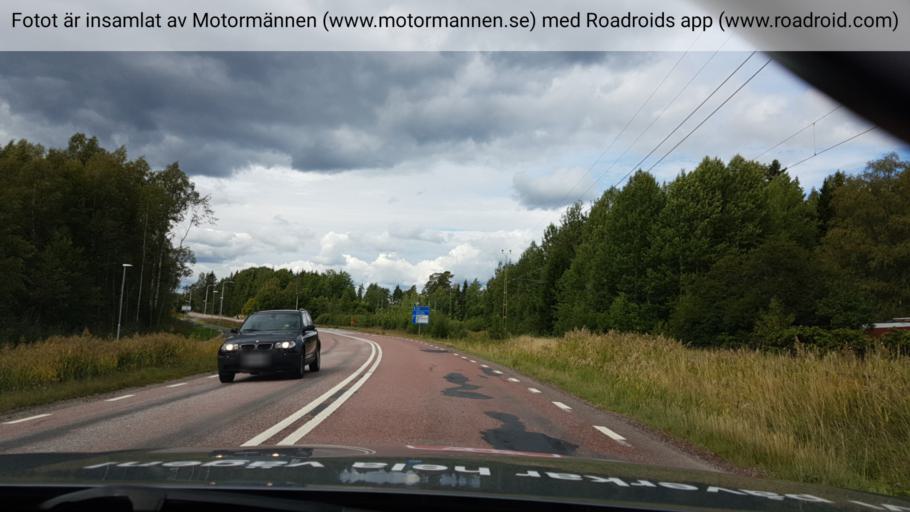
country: SE
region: Uppsala
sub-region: Heby Kommun
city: Morgongava
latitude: 59.9364
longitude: 16.9492
